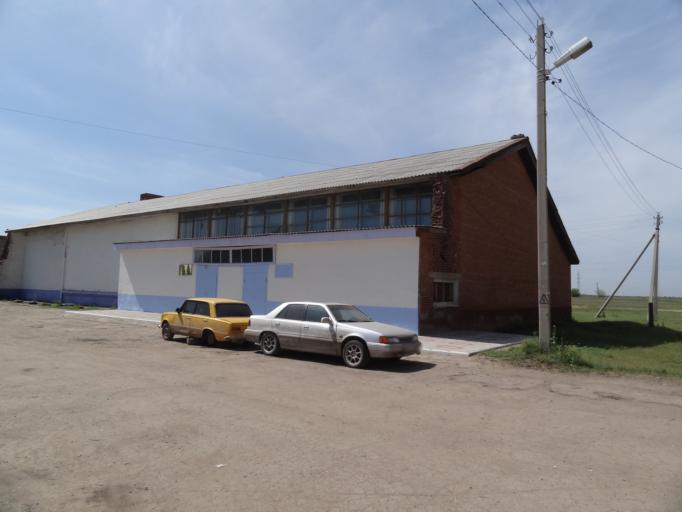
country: RU
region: Saratov
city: Engel's
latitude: 51.3740
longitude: 46.2154
